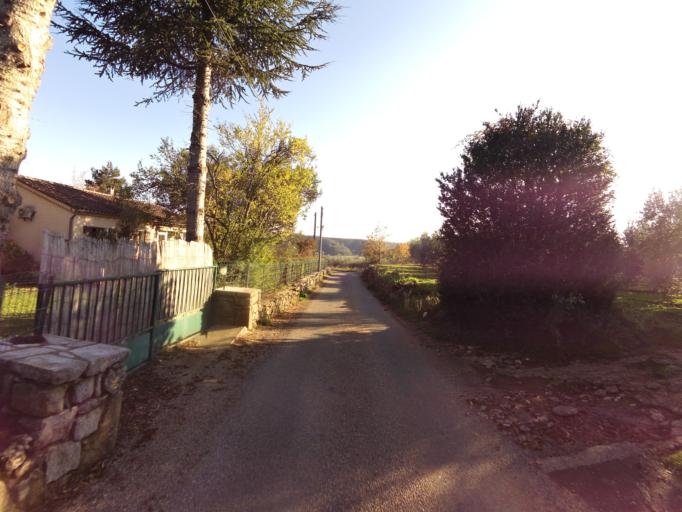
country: FR
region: Rhone-Alpes
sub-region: Departement de l'Ardeche
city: Largentiere
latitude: 44.5074
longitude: 4.2996
